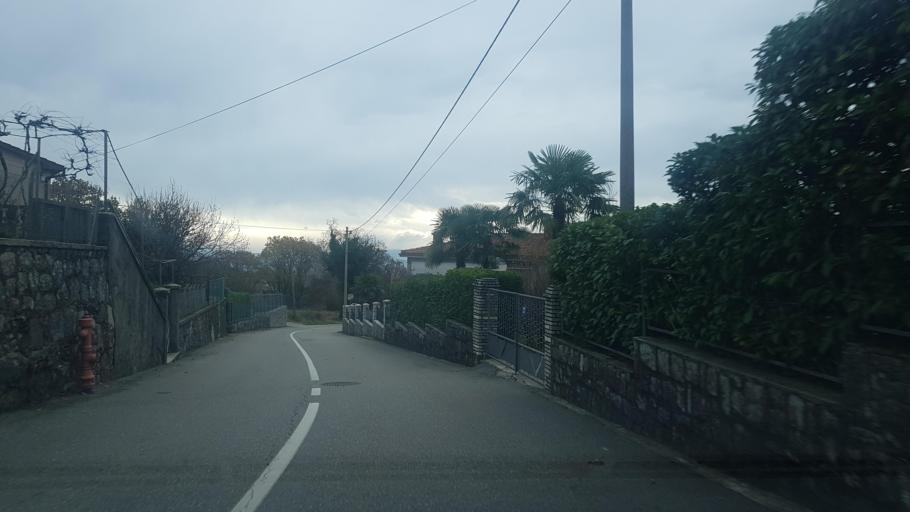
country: HR
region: Primorsko-Goranska
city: Matulji
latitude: 45.3687
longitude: 14.3240
